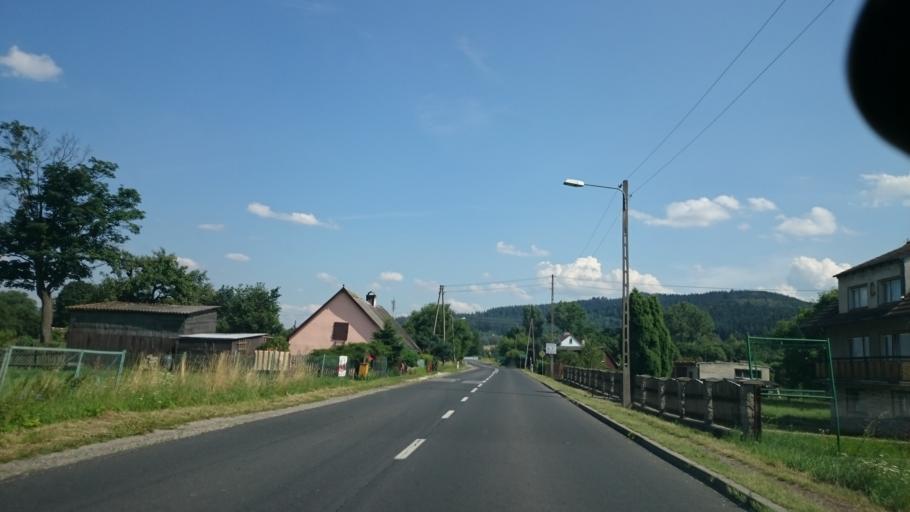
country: PL
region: Lower Silesian Voivodeship
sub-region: Powiat klodzki
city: Ladek-Zdroj
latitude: 50.3496
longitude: 16.7623
